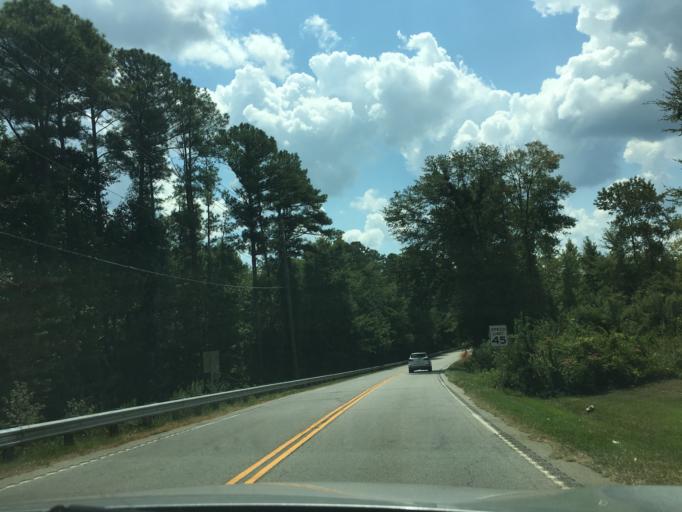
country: US
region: South Carolina
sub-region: Richland County
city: Lake Murray of Richland
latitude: 34.1221
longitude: -81.2302
